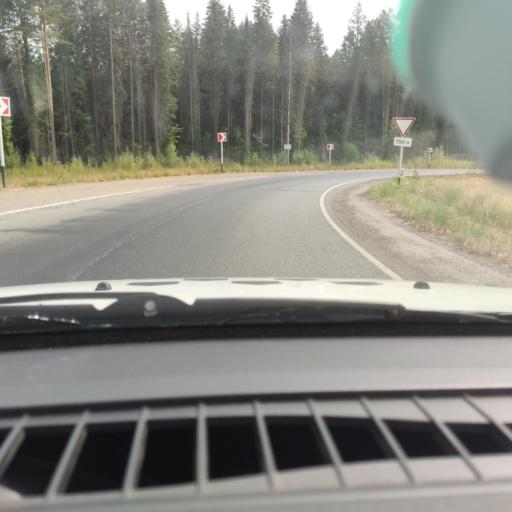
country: RU
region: Perm
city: Berezniki
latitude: 59.4065
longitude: 56.8833
